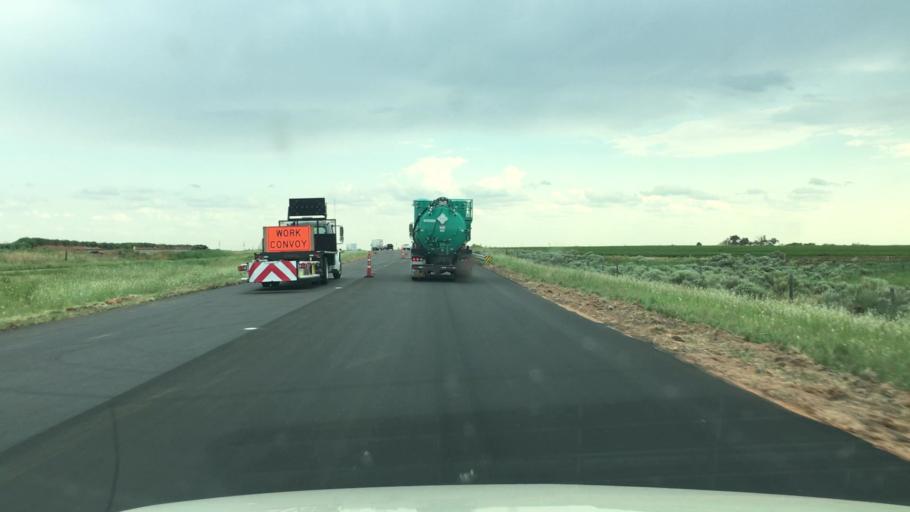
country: US
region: Texas
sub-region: Hall County
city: Memphis
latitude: 34.6339
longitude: -100.4767
